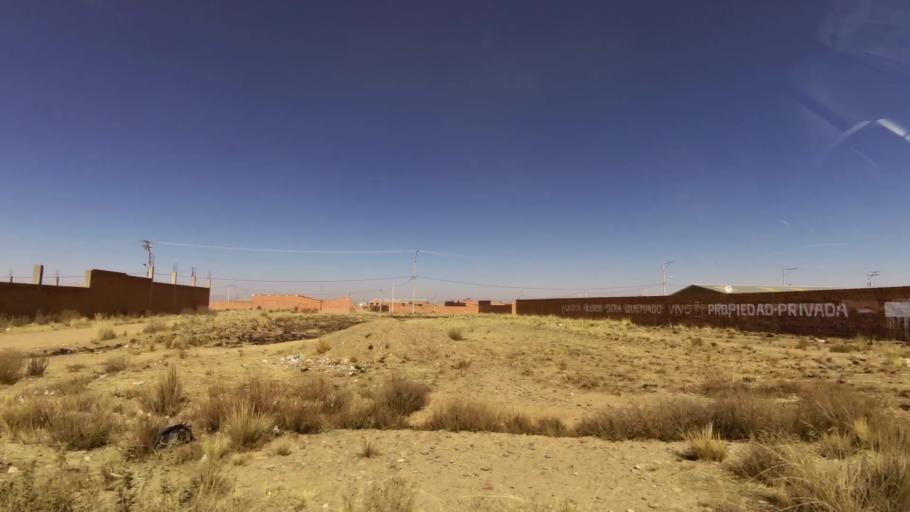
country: BO
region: La Paz
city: La Paz
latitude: -16.5807
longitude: -68.2155
